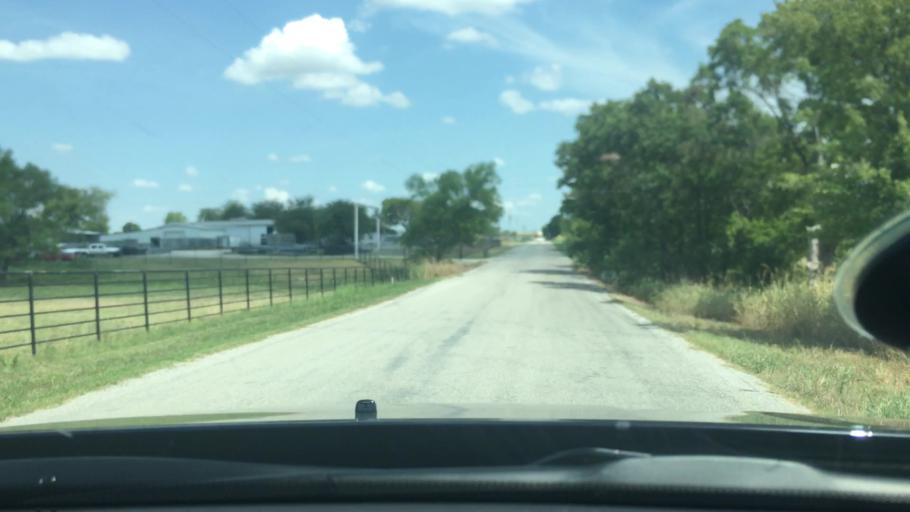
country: US
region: Oklahoma
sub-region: Love County
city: Marietta
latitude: 33.9457
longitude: -97.1869
